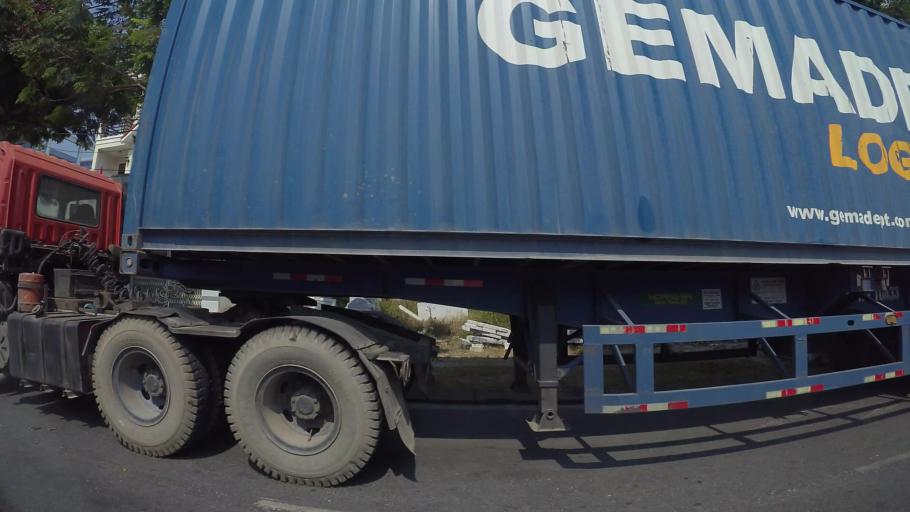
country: VN
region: Da Nang
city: Ngu Hanh Son
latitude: 16.0125
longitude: 108.2562
